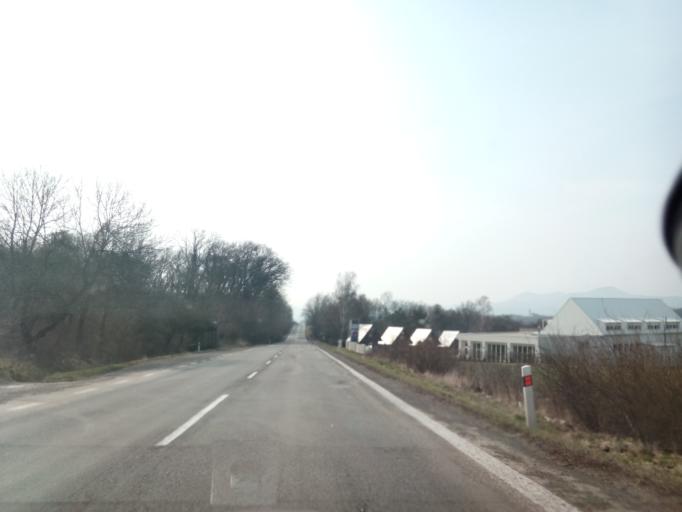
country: HU
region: Borsod-Abauj-Zemplen
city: Satoraljaujhely
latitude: 48.5062
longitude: 21.6547
